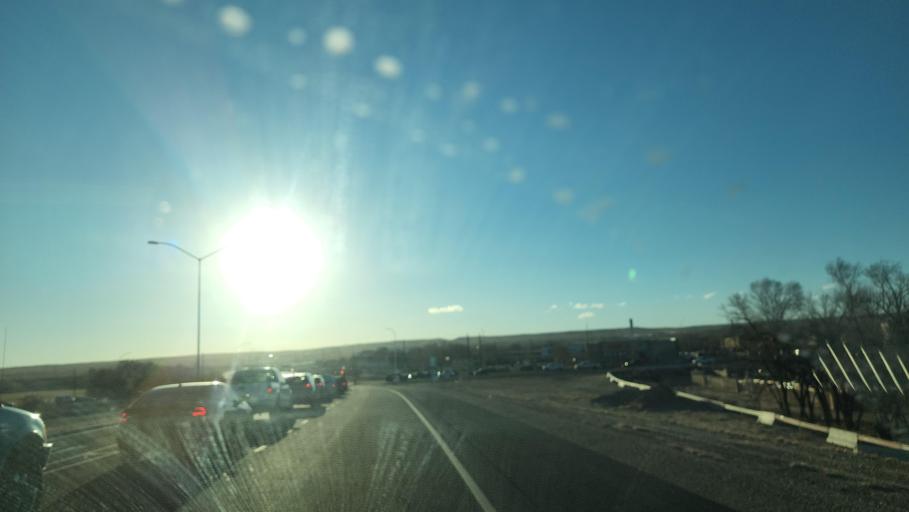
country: US
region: New Mexico
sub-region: Bernalillo County
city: South Valley
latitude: 35.0277
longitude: -106.7121
